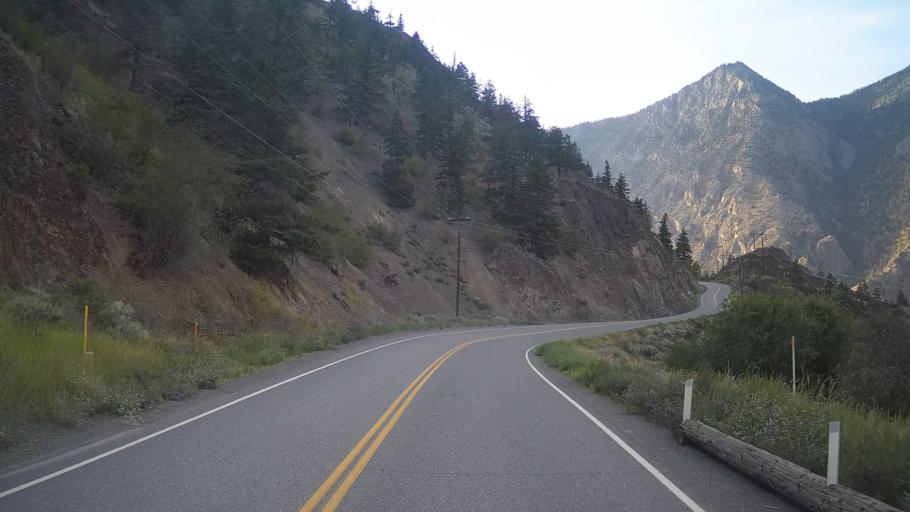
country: CA
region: British Columbia
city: Lillooet
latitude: 50.7500
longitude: -121.8925
